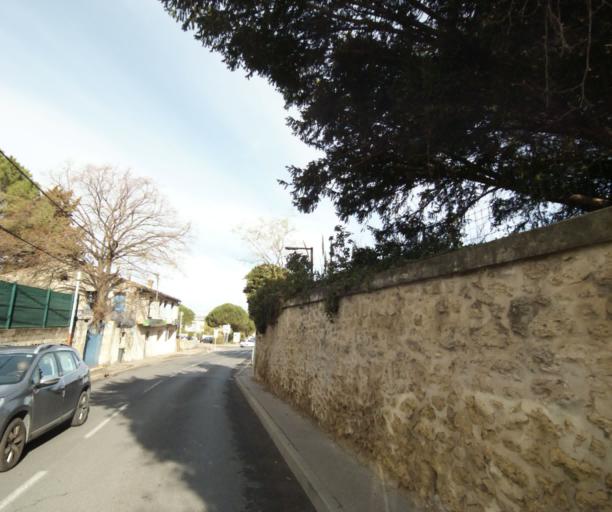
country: FR
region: Languedoc-Roussillon
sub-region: Departement de l'Herault
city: Saint-Jean-de-Vedas
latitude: 43.5788
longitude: 3.8243
